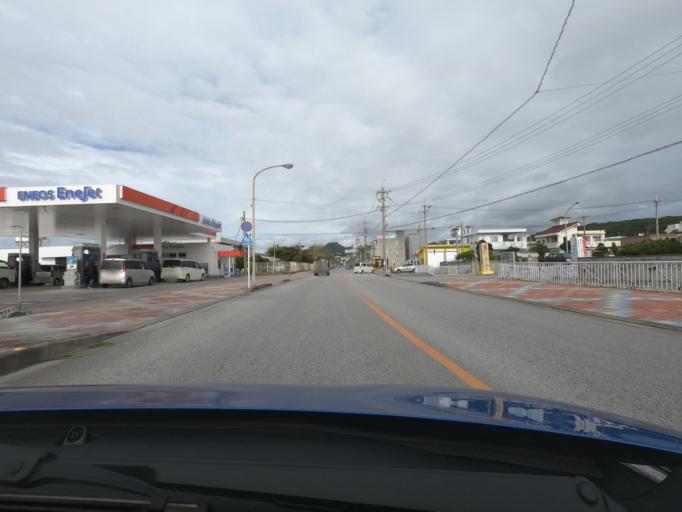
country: JP
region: Okinawa
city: Nago
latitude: 26.6537
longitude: 127.8806
